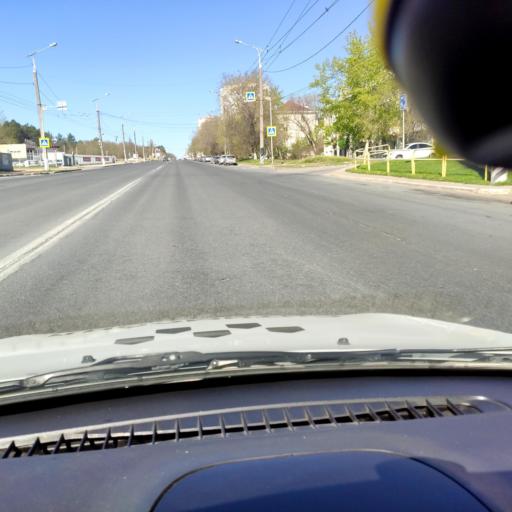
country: RU
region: Samara
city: Zhigulevsk
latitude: 53.4752
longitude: 49.4625
